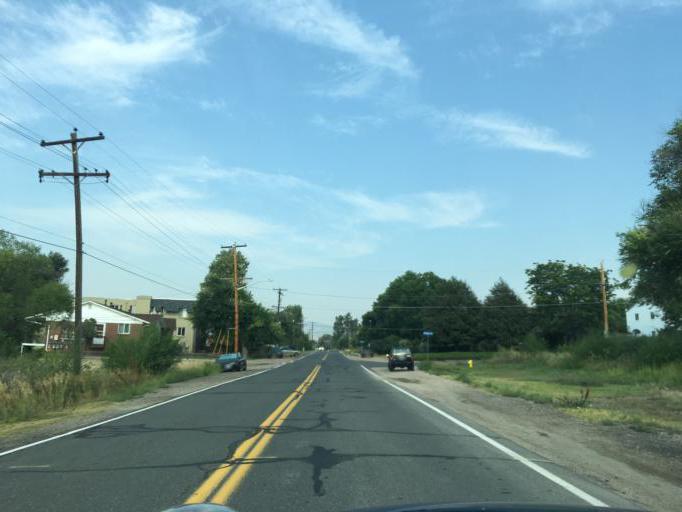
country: US
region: Colorado
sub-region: Jefferson County
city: Arvada
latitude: 39.8095
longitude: -105.0853
